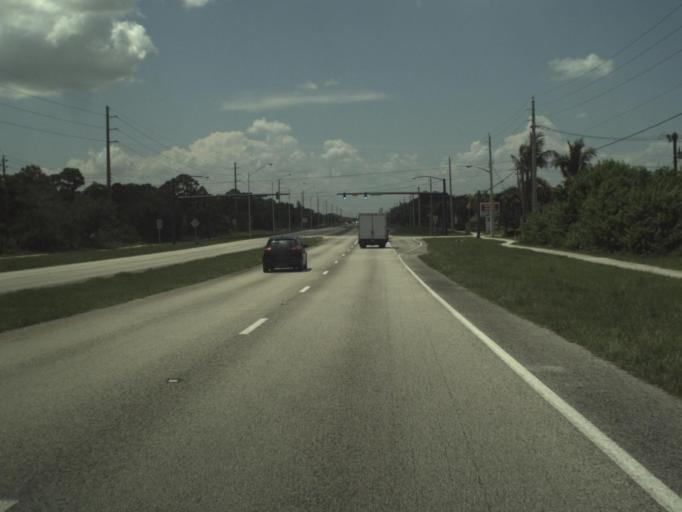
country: US
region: Florida
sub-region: Martin County
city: Hobe Sound
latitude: 27.0999
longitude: -80.1602
